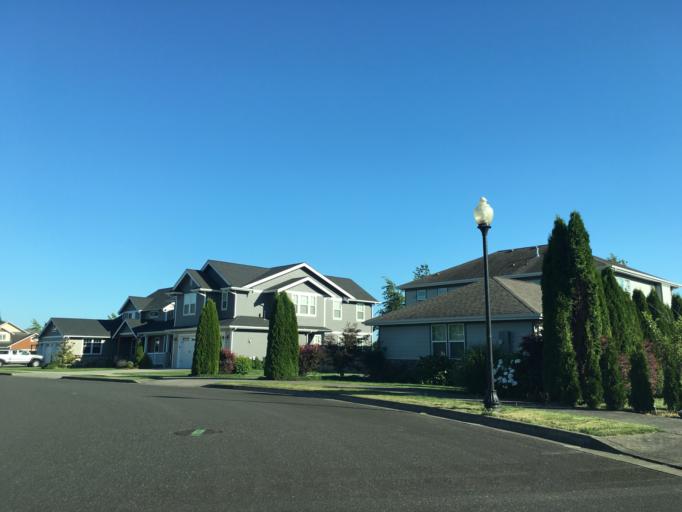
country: US
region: Washington
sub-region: Whatcom County
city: Lynden
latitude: 48.9623
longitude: -122.4611
